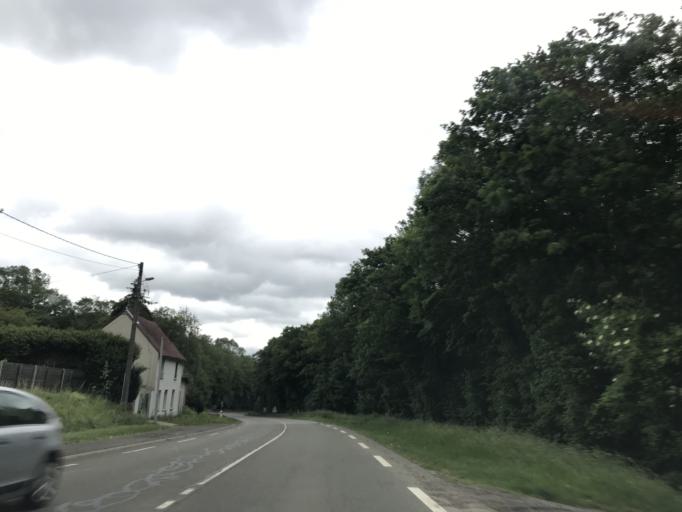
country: FR
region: Ile-de-France
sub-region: Departement des Yvelines
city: Bennecourt
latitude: 49.0261
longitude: 1.5382
